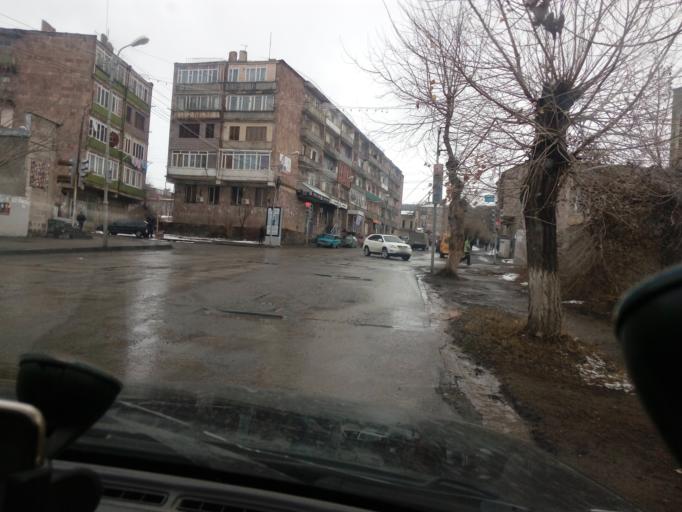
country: AM
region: Kotayk'i Marz
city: Hrazdan
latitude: 40.4952
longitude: 44.7586
